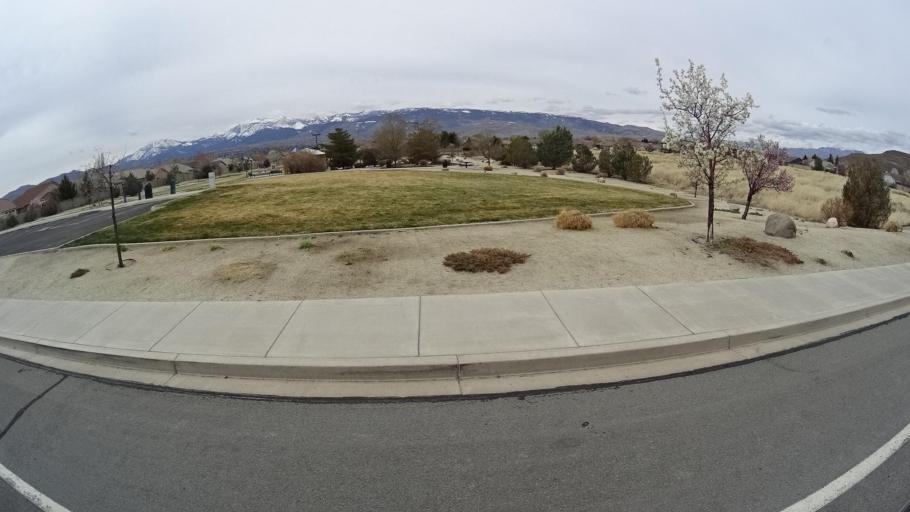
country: US
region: Nevada
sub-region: Washoe County
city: Sparks
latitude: 39.4438
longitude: -119.7363
